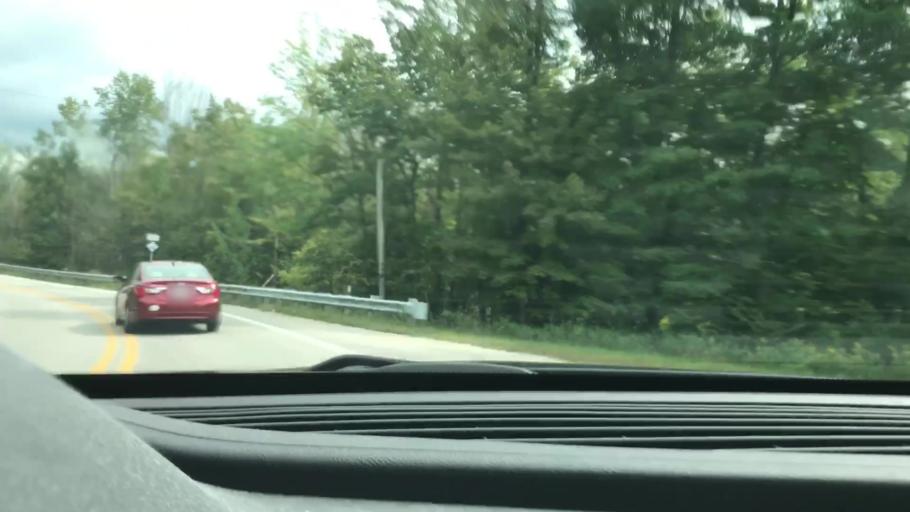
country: US
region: Michigan
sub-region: Antrim County
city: Bellaire
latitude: 45.0790
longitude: -85.2824
